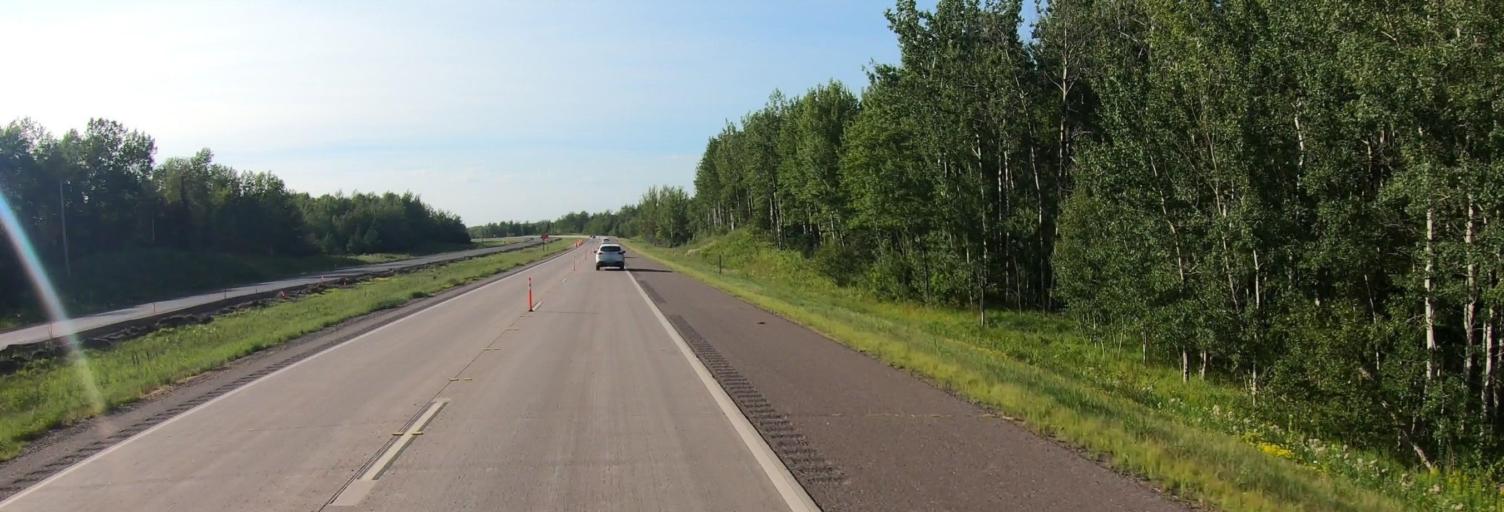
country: US
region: Minnesota
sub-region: Saint Louis County
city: Hermantown
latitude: 46.9171
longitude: -92.3986
